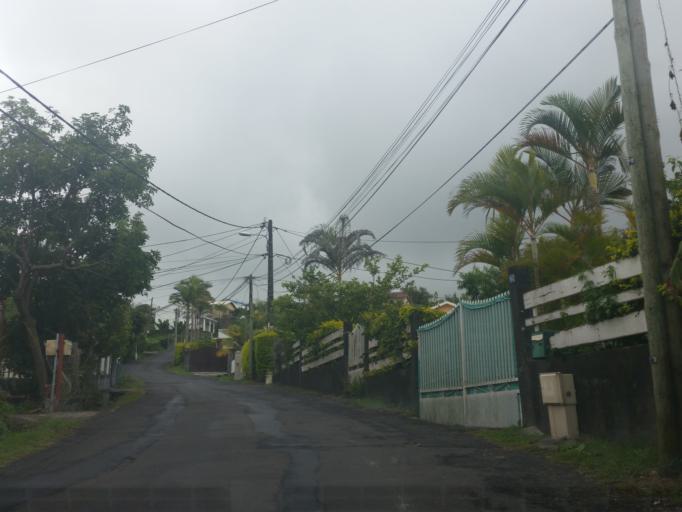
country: RE
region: Reunion
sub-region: Reunion
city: Le Tampon
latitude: -21.2375
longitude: 55.5194
